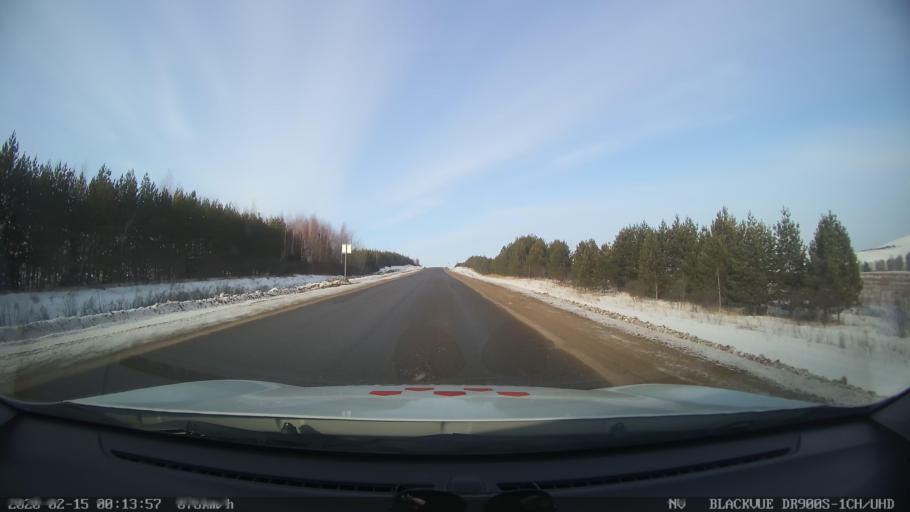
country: RU
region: Tatarstan
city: Stolbishchi
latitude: 55.4806
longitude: 49.0044
